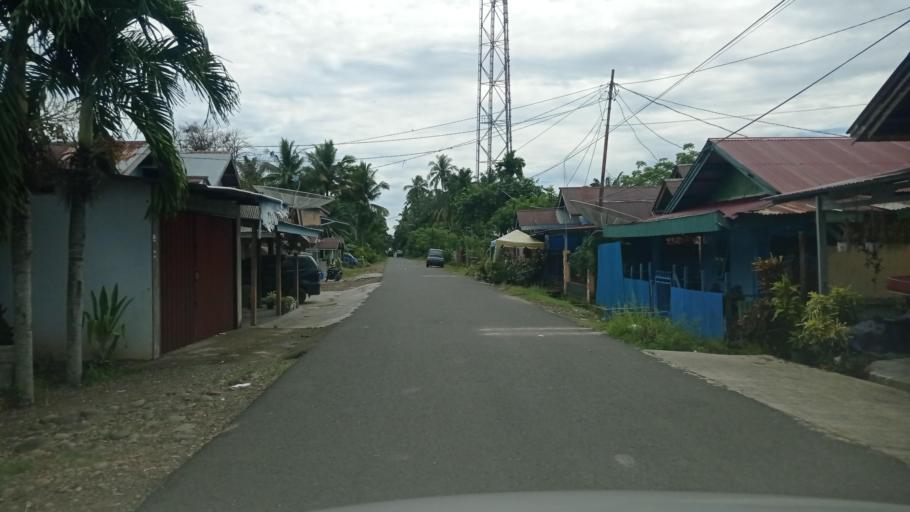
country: ID
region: Bengkulu
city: Ipuh
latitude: -2.5805
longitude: 101.1172
